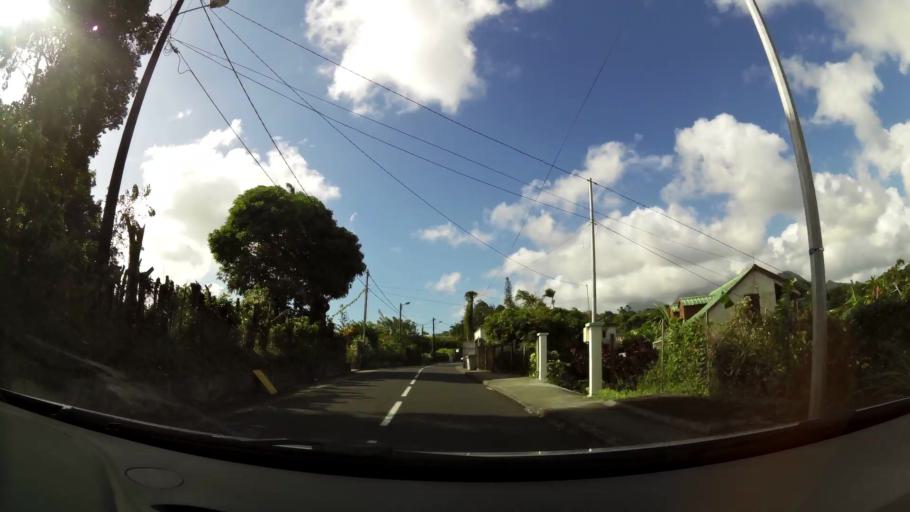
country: MQ
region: Martinique
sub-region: Martinique
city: Fort-de-France
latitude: 14.6428
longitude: -61.0773
